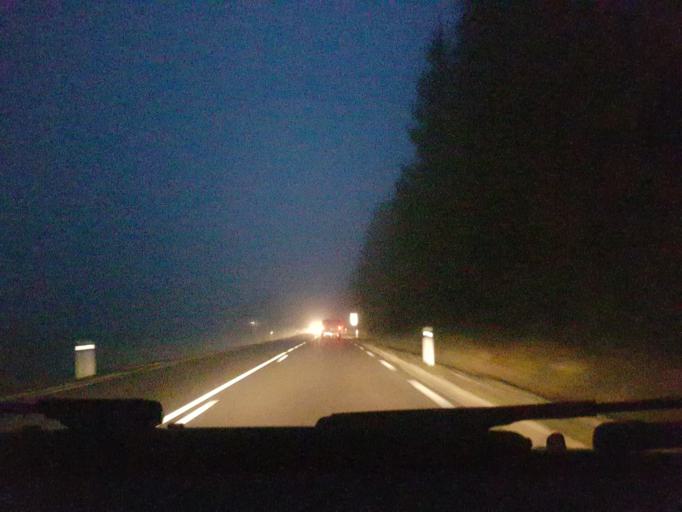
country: FR
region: Franche-Comte
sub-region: Departement du Doubs
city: Doubs
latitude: 46.9721
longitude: 6.3445
